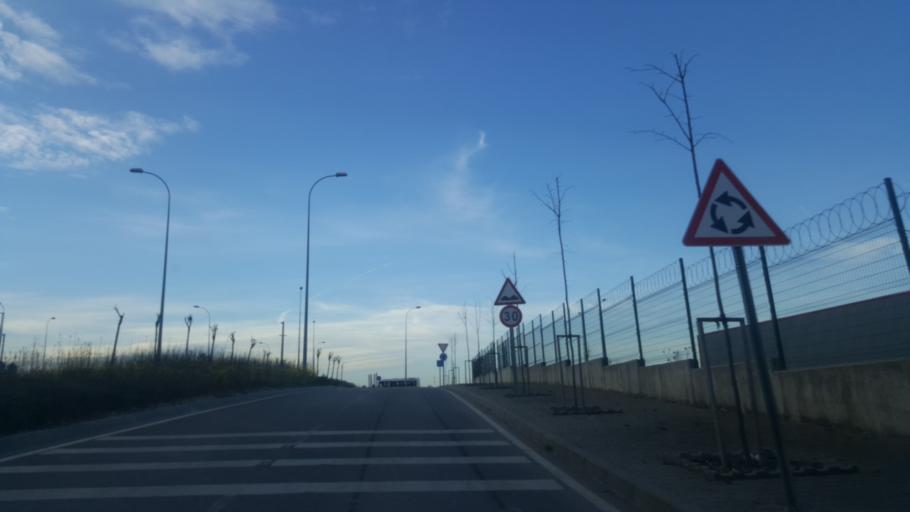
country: TR
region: Kocaeli
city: Tavsanli
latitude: 40.8369
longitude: 29.5493
